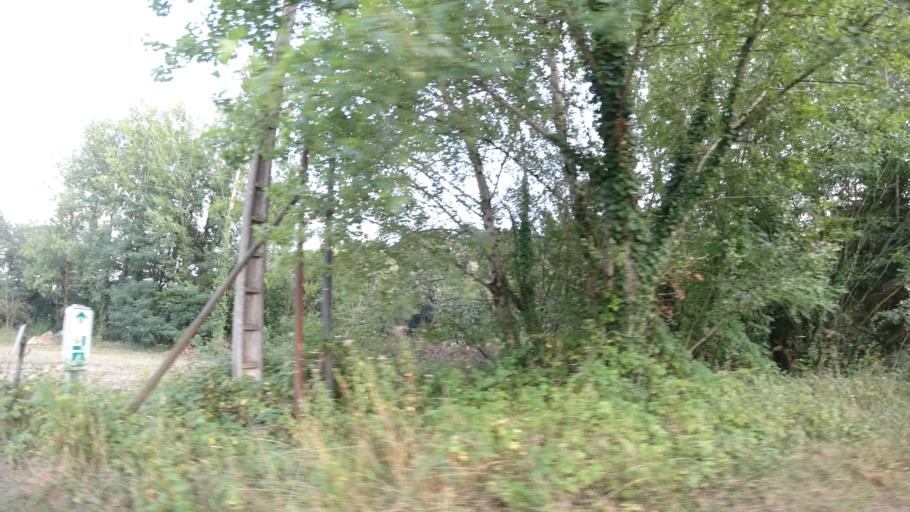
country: FR
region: Midi-Pyrenees
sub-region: Departement de l'Aveyron
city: Livinhac-le-Haut
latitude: 44.5999
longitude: 2.2387
